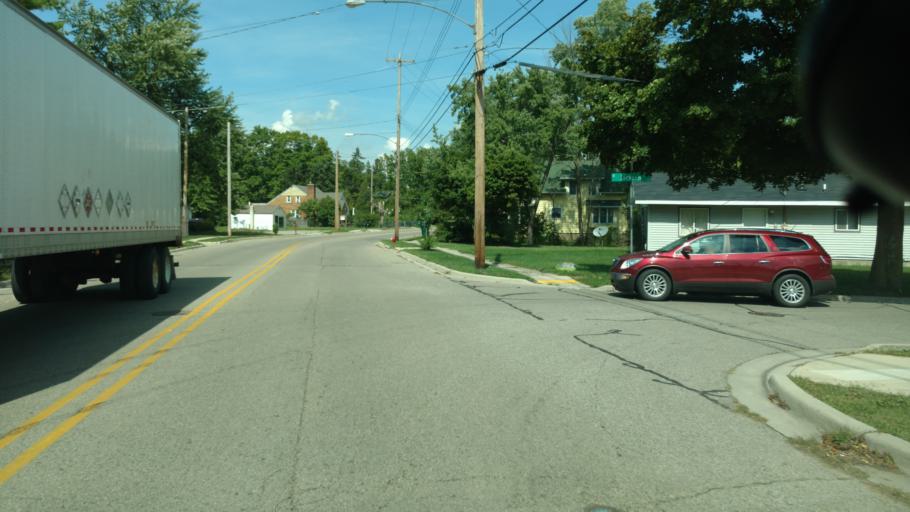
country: US
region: Michigan
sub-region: Ingham County
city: Lansing
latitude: 42.7622
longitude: -84.5554
